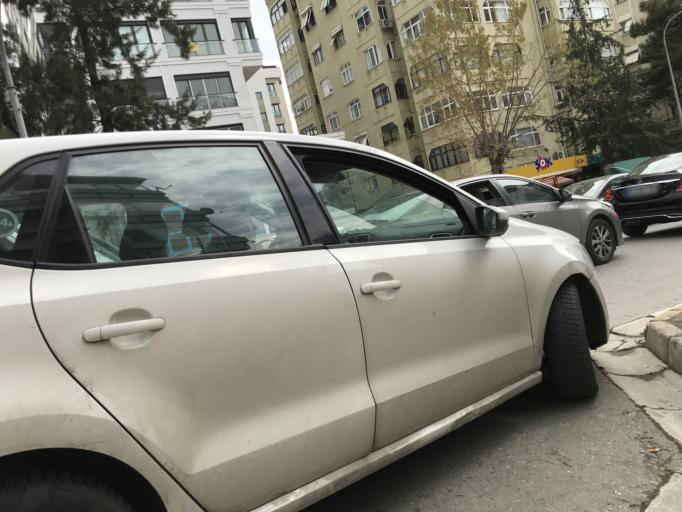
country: TR
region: Istanbul
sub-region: Atasehir
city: Atasehir
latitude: 40.9742
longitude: 29.0632
